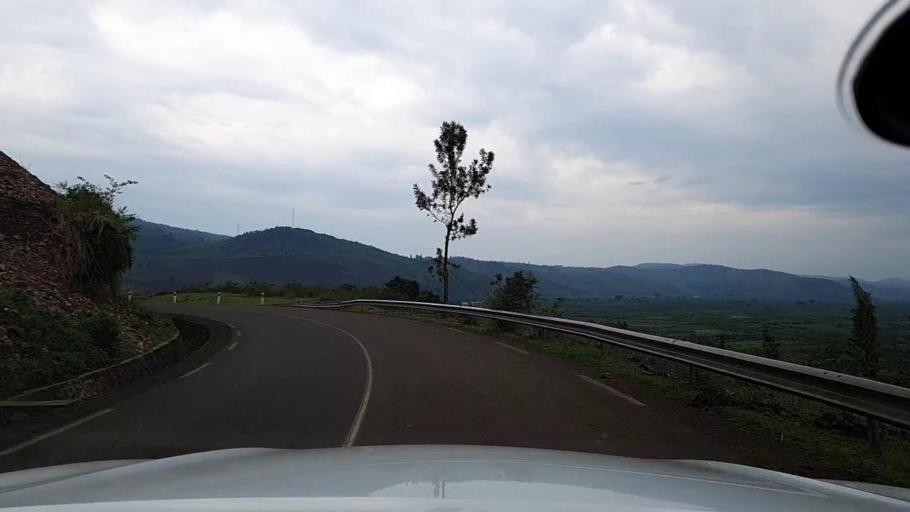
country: BI
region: Cibitoke
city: Cibitoke
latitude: -2.7349
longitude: 29.0361
